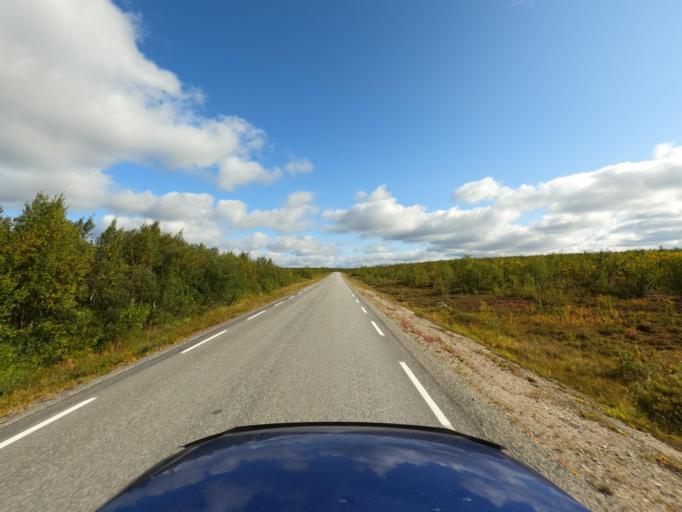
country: NO
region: Finnmark Fylke
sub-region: Porsanger
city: Lakselv
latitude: 69.3920
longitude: 24.5465
